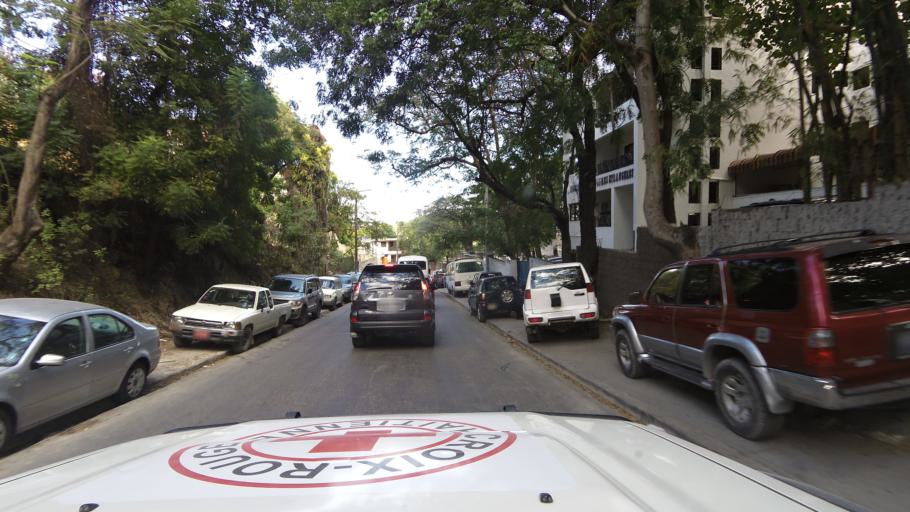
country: HT
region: Ouest
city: Delmas 73
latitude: 18.5300
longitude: -72.2961
